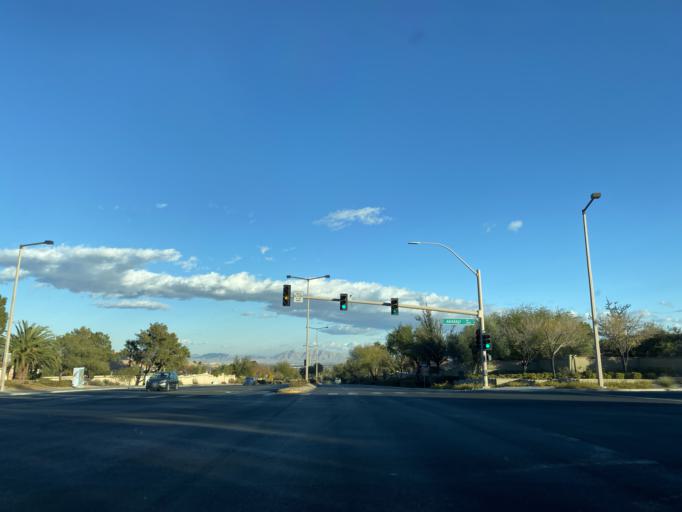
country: US
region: Nevada
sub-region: Clark County
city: Summerlin South
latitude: 36.2051
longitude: -115.3202
